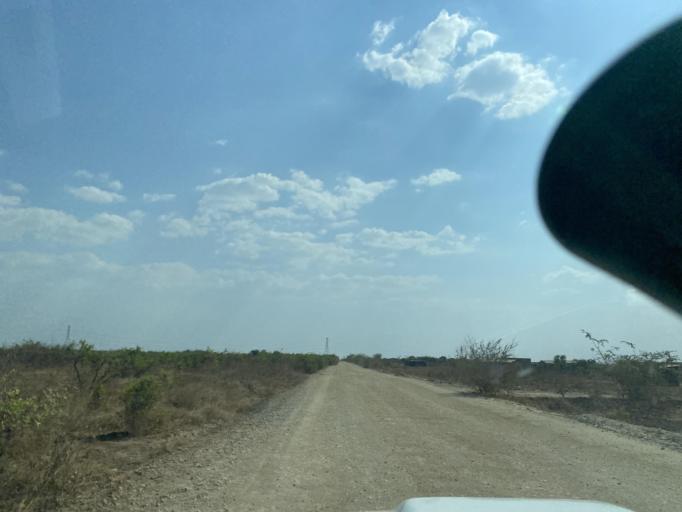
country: ZM
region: Lusaka
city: Lusaka
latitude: -15.3635
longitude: 28.0898
